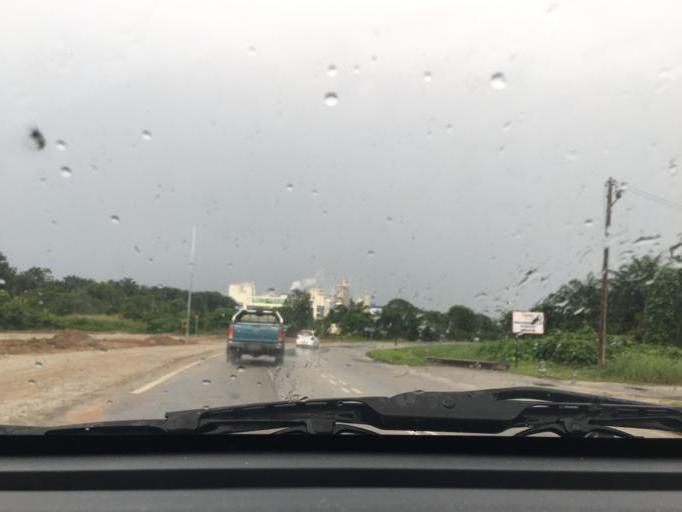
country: MY
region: Kedah
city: Sungai Petani
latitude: 5.6045
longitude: 100.6404
